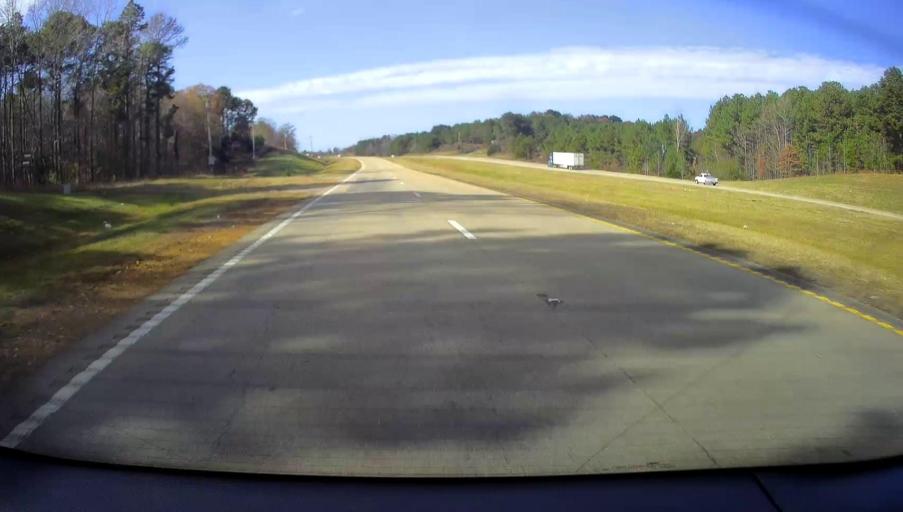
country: US
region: Mississippi
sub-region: Tippah County
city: Ripley
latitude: 34.9533
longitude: -88.9512
